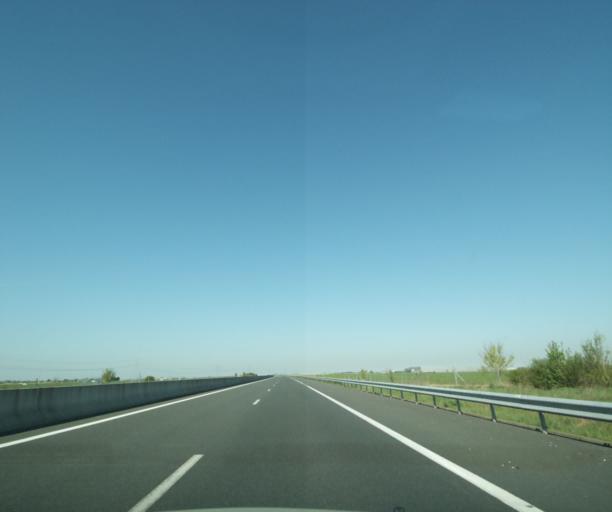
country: FR
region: Centre
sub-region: Departement du Loiret
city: Dadonville
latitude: 48.1133
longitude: 2.2665
